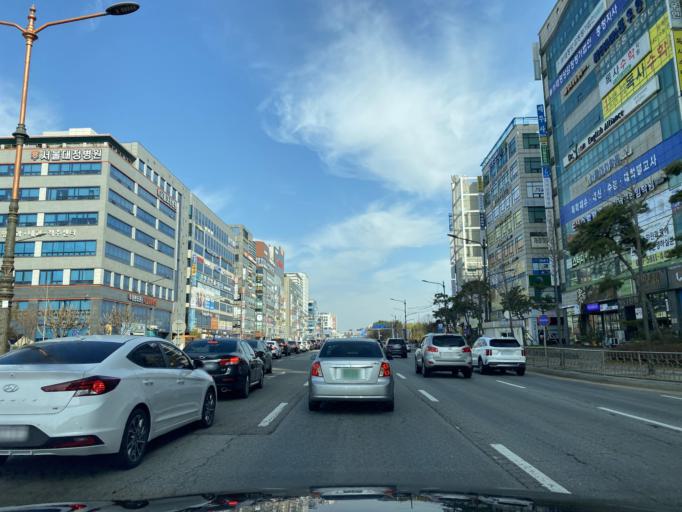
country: KR
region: Chungcheongnam-do
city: Cheonan
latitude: 36.8107
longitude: 127.1083
